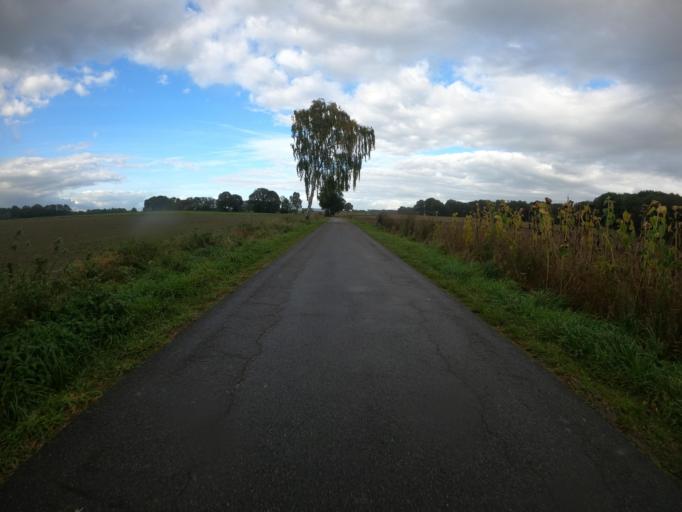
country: DE
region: North Rhine-Westphalia
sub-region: Regierungsbezirk Dusseldorf
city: Schermbeck
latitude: 51.7259
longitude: 6.8723
